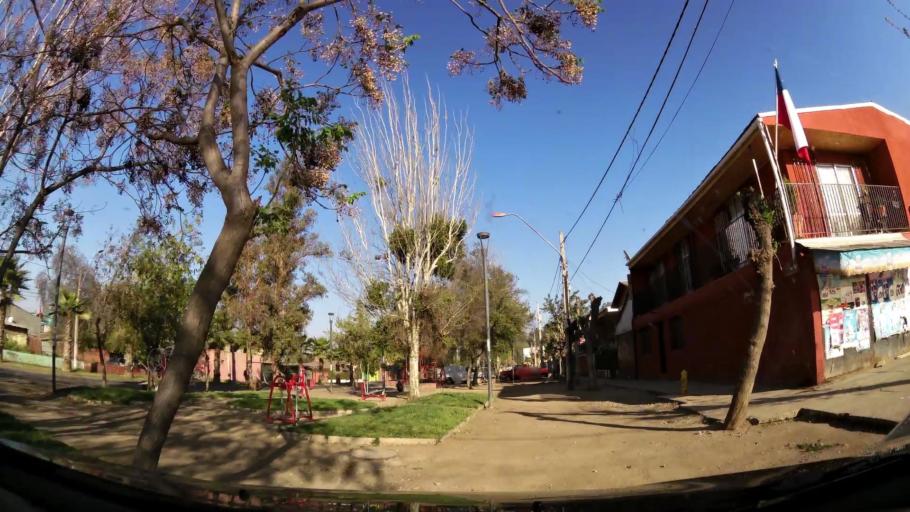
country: CL
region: Santiago Metropolitan
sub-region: Provincia de Santiago
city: Santiago
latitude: -33.3724
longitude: -70.6406
